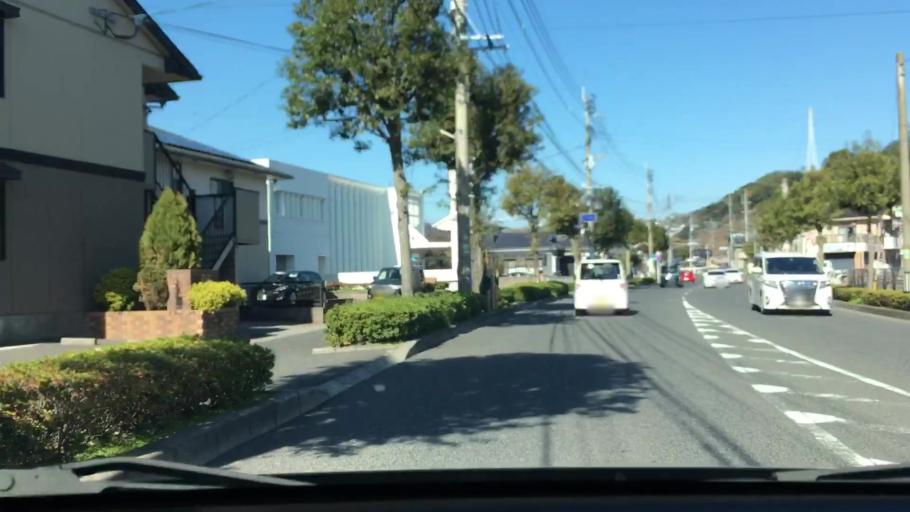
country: JP
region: Kagoshima
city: Kagoshima-shi
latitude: 31.5466
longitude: 130.5336
